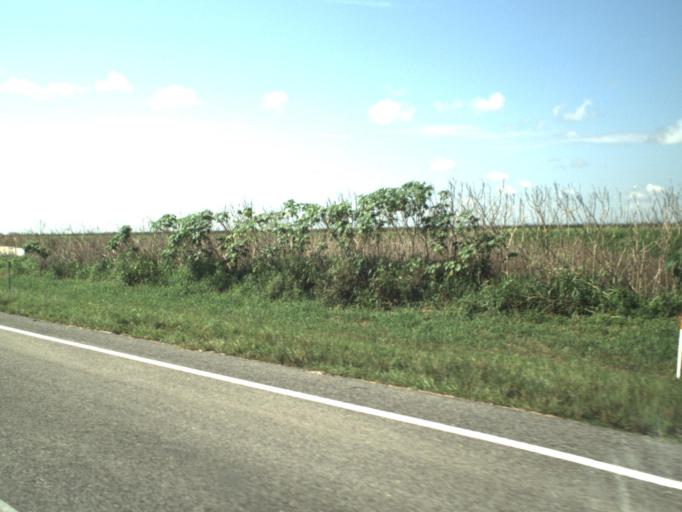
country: US
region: Florida
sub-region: Palm Beach County
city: Belle Glade Camp
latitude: 26.3703
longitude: -80.5654
